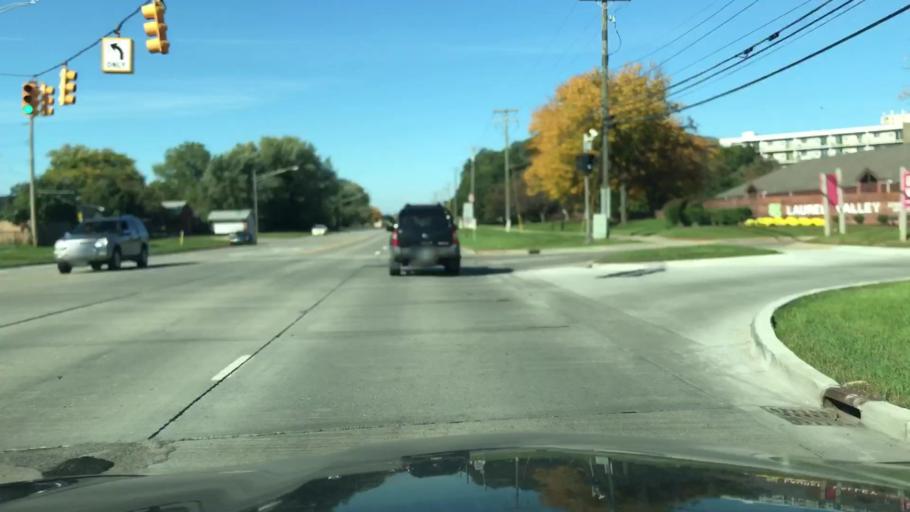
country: US
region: Michigan
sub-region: Macomb County
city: Sterling Heights
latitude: 42.5574
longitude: -83.0884
